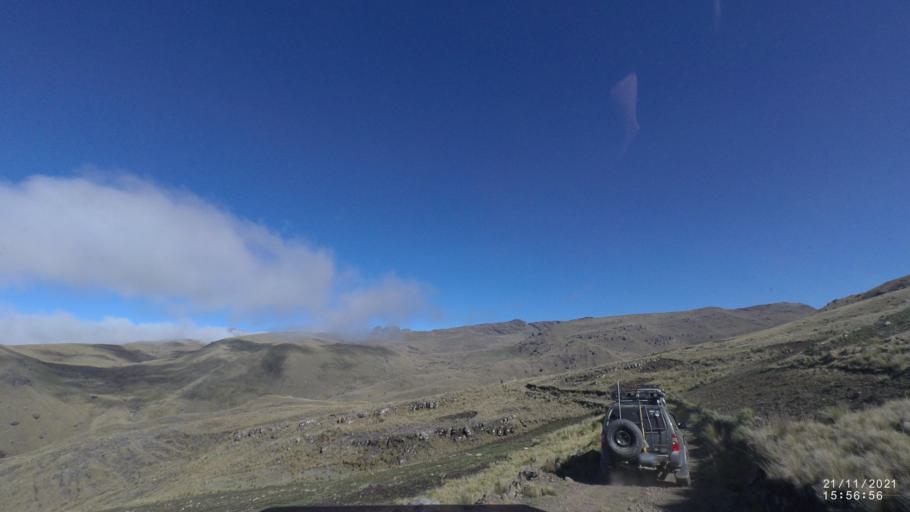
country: BO
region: Cochabamba
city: Cochabamba
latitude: -16.9757
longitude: -66.2650
